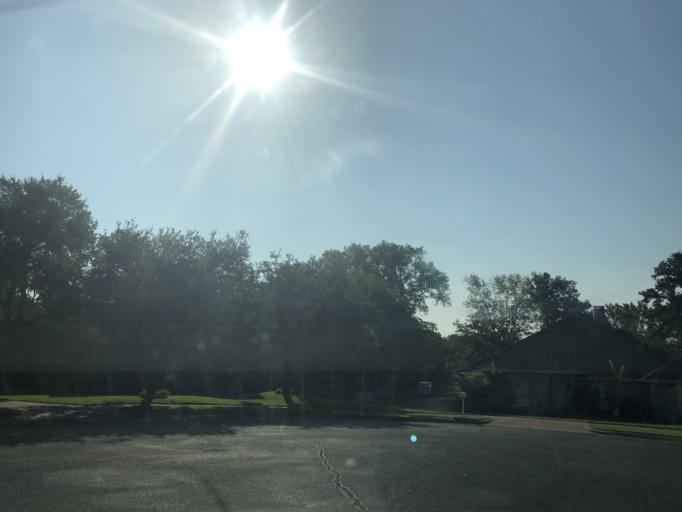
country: US
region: Texas
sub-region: Tarrant County
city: Euless
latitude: 32.8733
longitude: -97.0870
